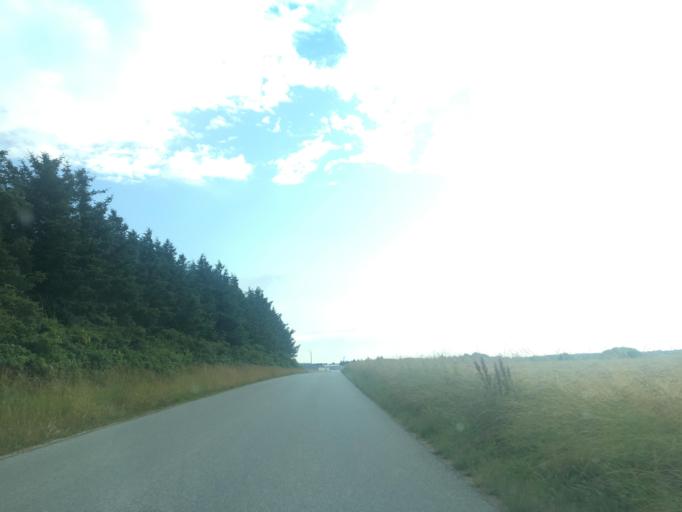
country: DK
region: North Denmark
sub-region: Thisted Kommune
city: Hurup
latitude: 56.7560
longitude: 8.4380
